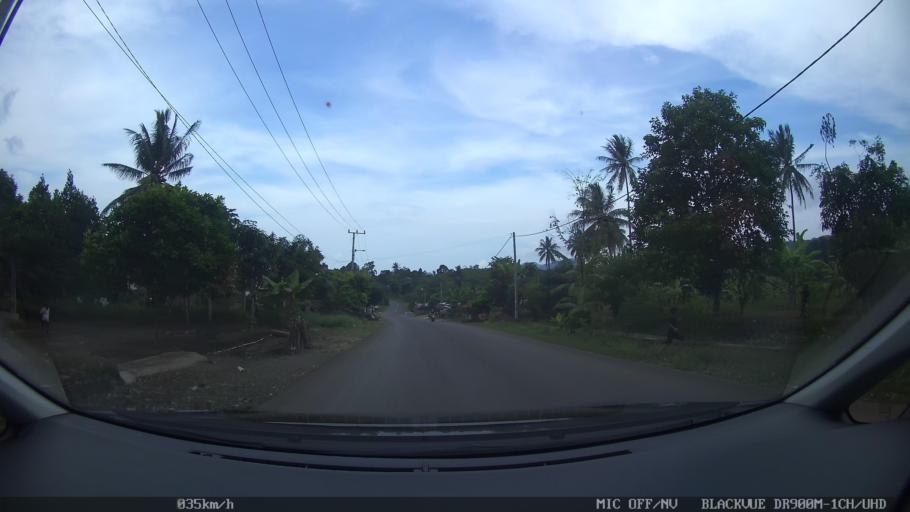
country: ID
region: Lampung
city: Bandarlampung
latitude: -5.4247
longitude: 105.1951
